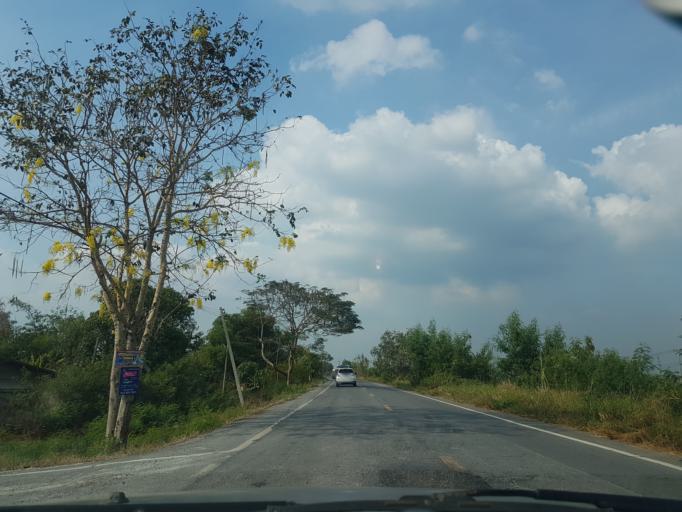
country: TH
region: Phra Nakhon Si Ayutthaya
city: Phachi
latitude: 14.4225
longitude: 100.7798
